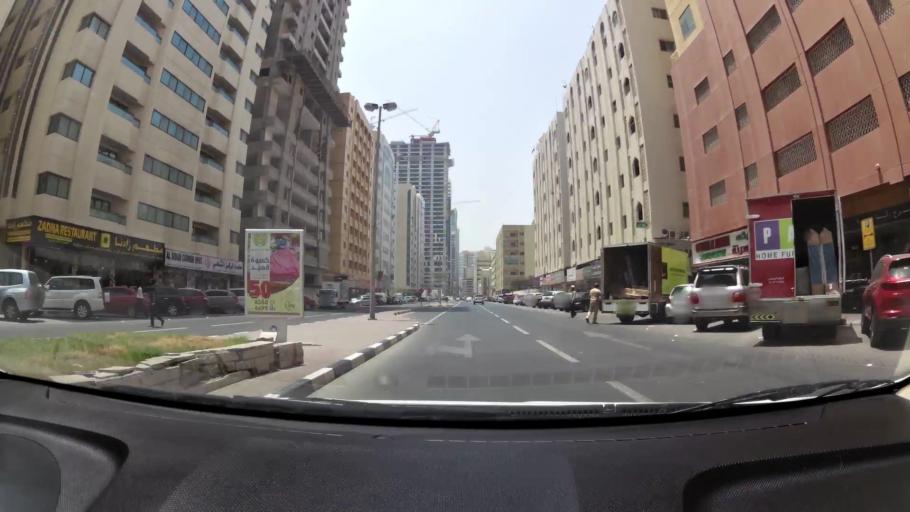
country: AE
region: Ash Shariqah
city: Sharjah
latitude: 25.3293
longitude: 55.3930
